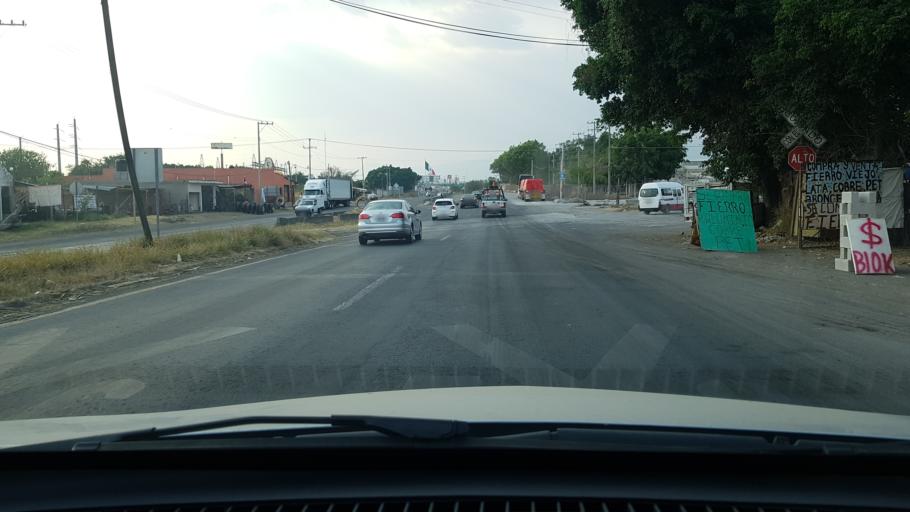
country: MX
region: Morelos
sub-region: Cuautla
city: Tierra Larga (Campo Nuevo)
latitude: 18.8450
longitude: -98.9295
